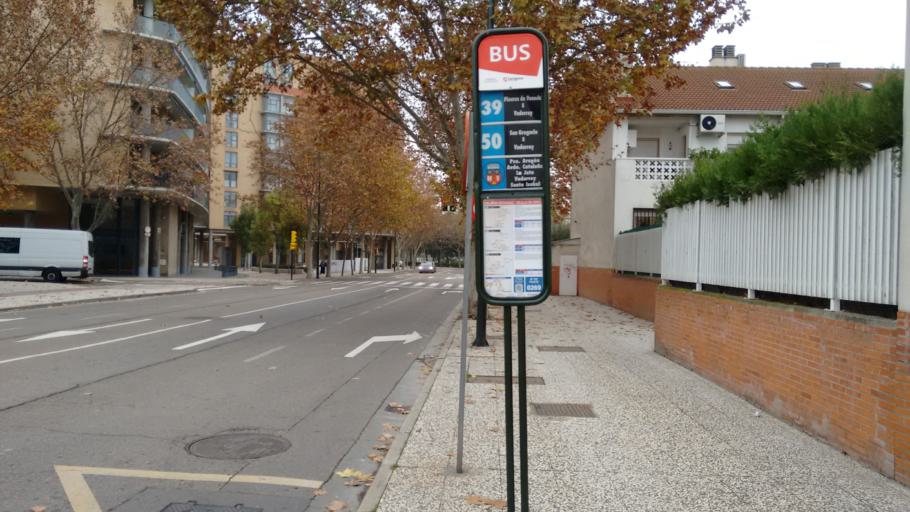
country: ES
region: Aragon
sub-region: Provincia de Zaragoza
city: Zaragoza
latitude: 41.6592
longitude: -0.8591
